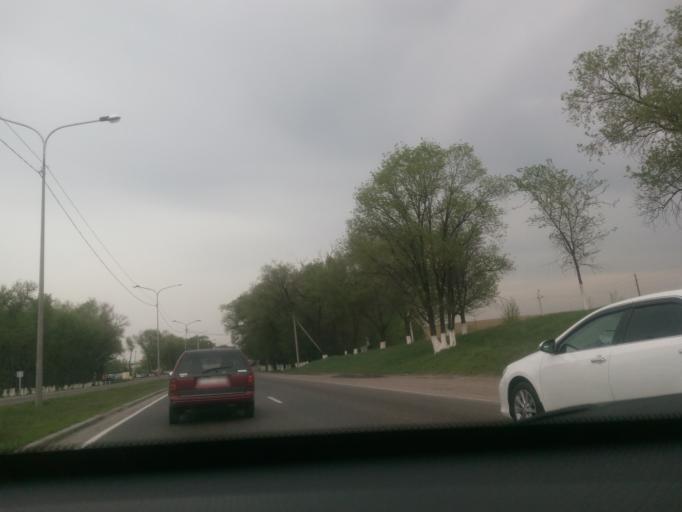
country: KZ
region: Almaty Oblysy
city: Burunday
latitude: 43.2229
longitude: 76.7203
